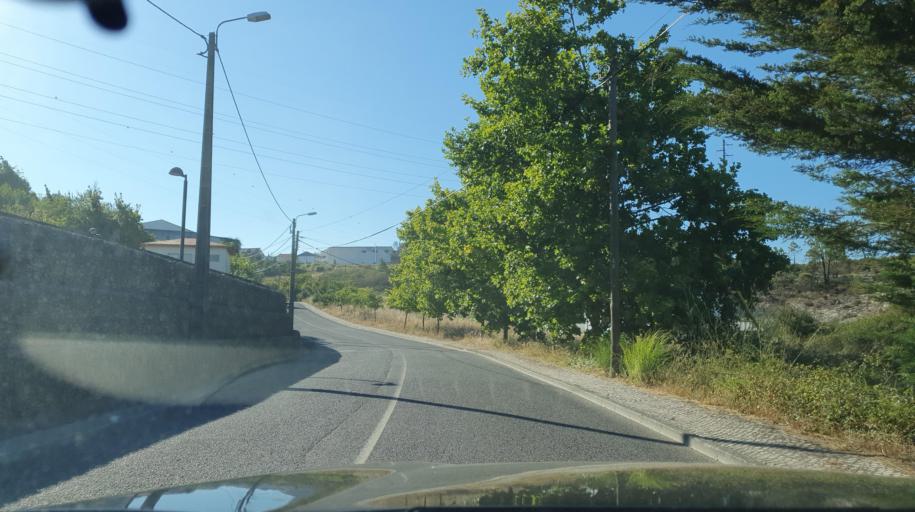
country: PT
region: Lisbon
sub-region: Sintra
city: Belas
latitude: 38.7953
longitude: -9.2462
